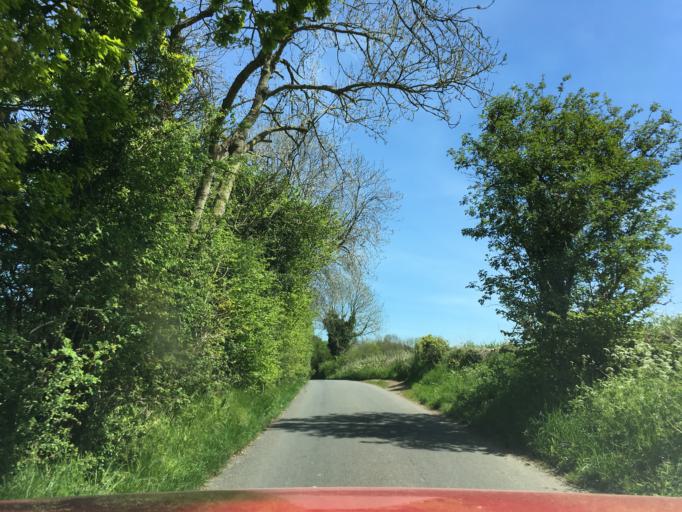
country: GB
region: England
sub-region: Gloucestershire
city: Chalford
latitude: 51.7228
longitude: -2.1084
